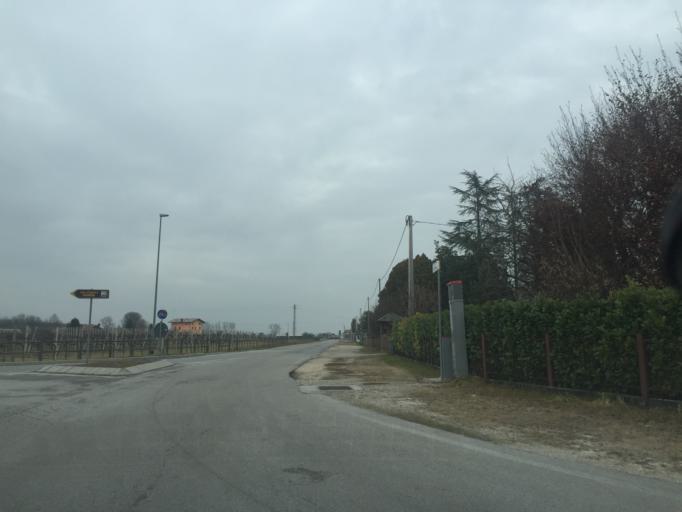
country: IT
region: Friuli Venezia Giulia
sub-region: Provincia di Pordenone
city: Cavolano-Schiavoi
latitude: 45.9371
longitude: 12.5196
